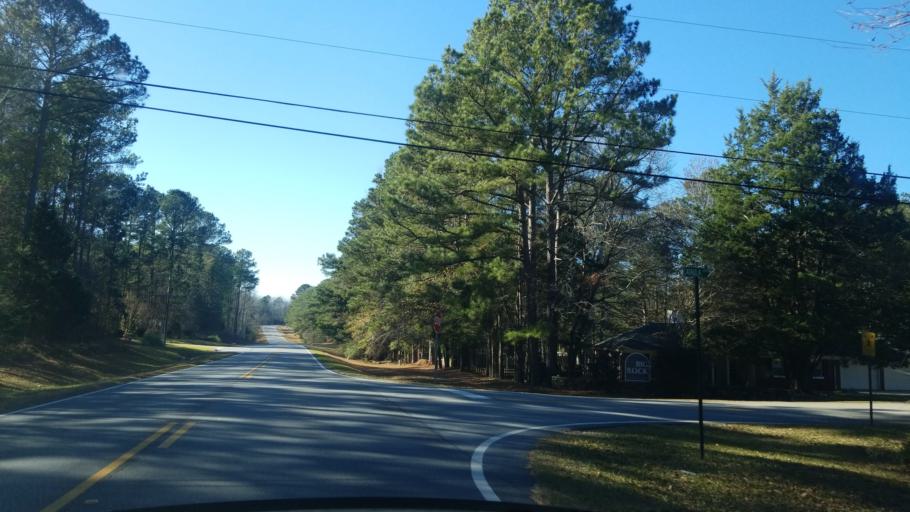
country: US
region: Georgia
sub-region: Harris County
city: Hamilton
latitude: 32.6676
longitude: -84.8842
